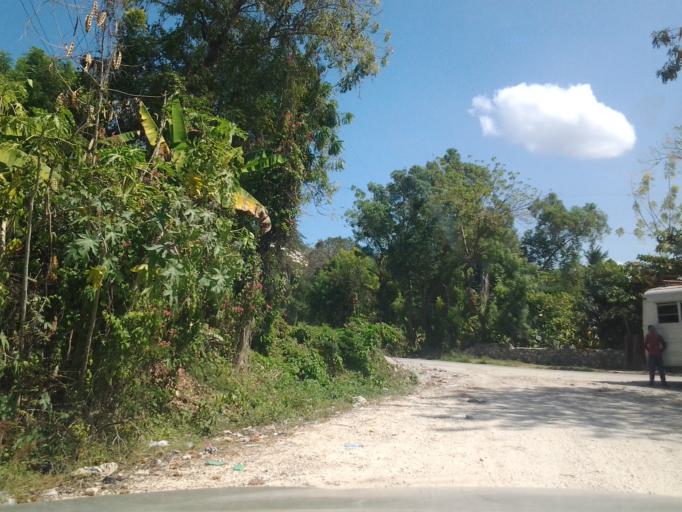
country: HT
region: Ouest
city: Tigwav
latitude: 18.4401
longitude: -72.8393
